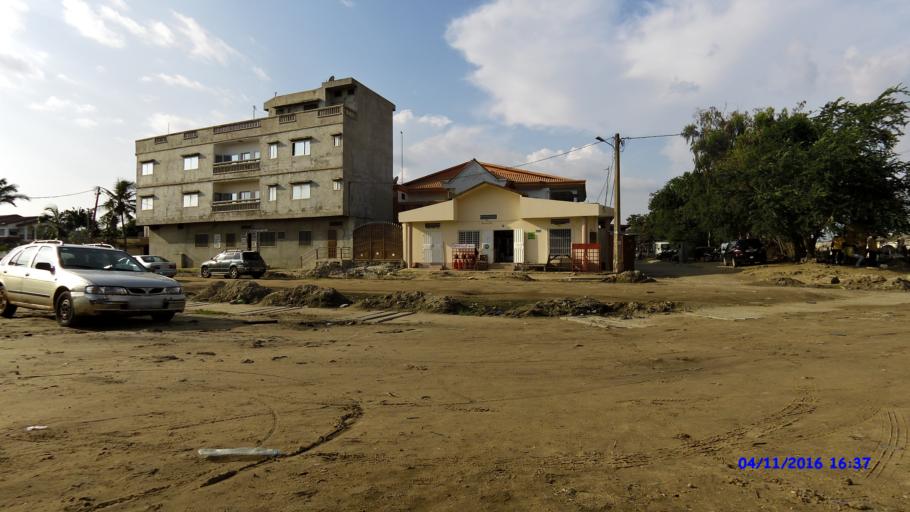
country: BJ
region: Littoral
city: Cotonou
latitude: 6.3692
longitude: 2.3936
